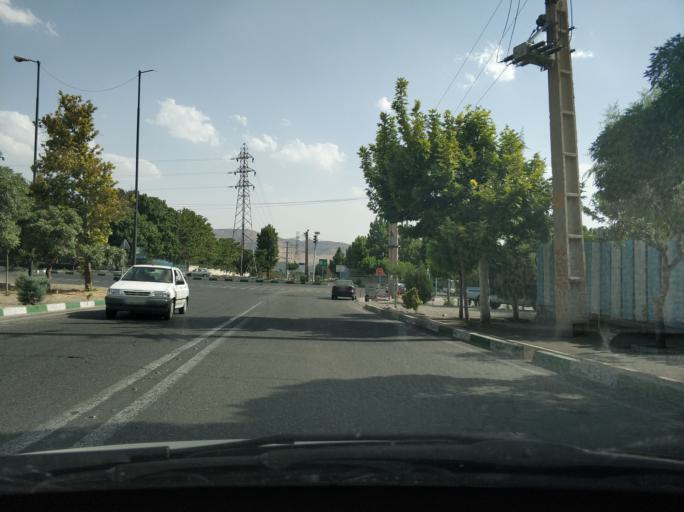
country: IR
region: Tehran
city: Tajrish
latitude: 35.7456
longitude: 51.5765
